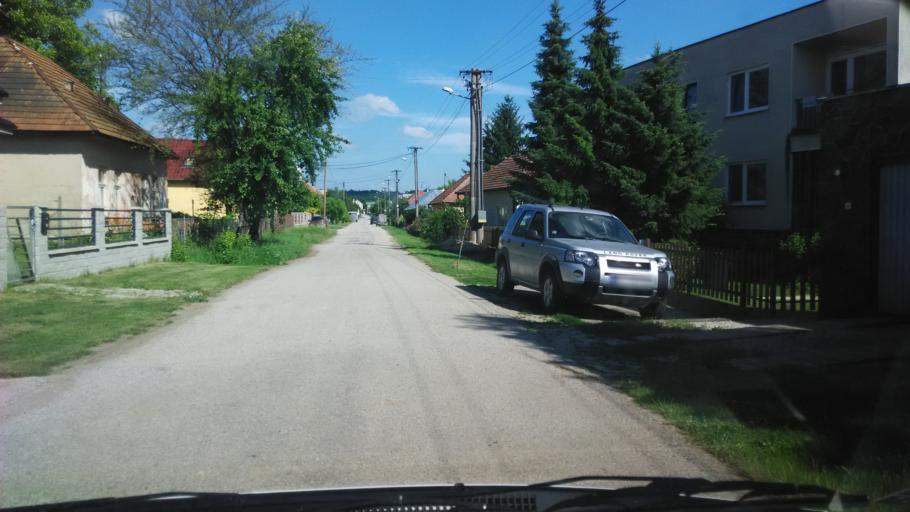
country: SK
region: Nitriansky
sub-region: Okres Nitra
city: Vrable
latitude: 48.1155
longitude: 18.3789
